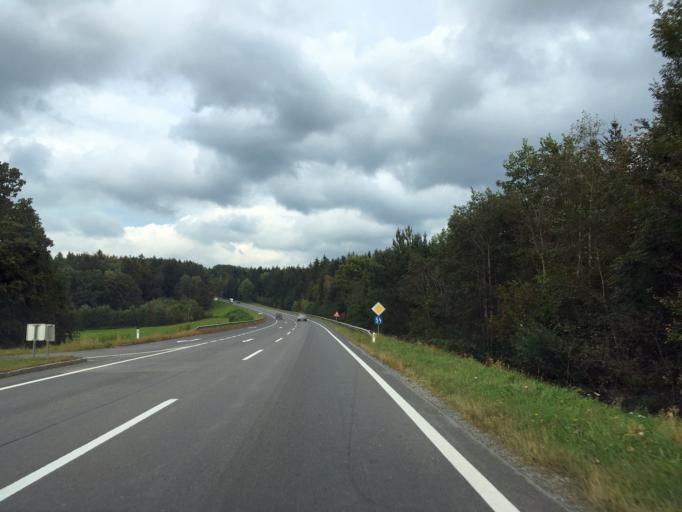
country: AT
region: Styria
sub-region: Politischer Bezirk Hartberg-Fuerstenfeld
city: Friedberg
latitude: 47.4194
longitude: 16.0502
